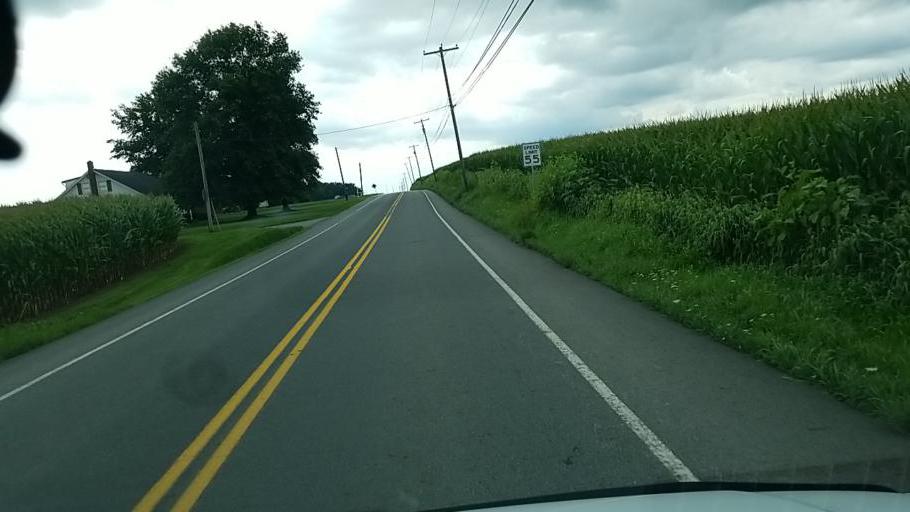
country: US
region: Pennsylvania
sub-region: Dauphin County
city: Elizabethville
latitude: 40.6006
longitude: -76.8181
